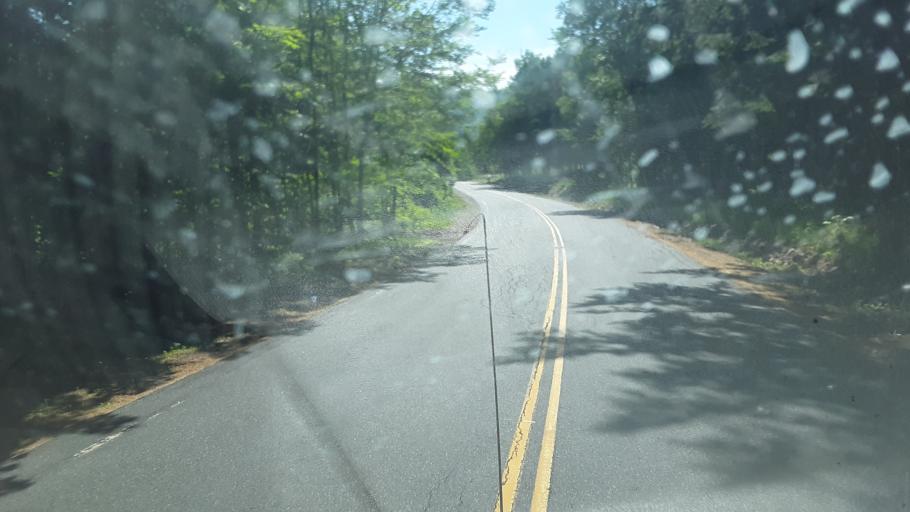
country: US
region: New Hampshire
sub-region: Grafton County
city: North Haverhill
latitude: 44.0979
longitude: -71.8616
